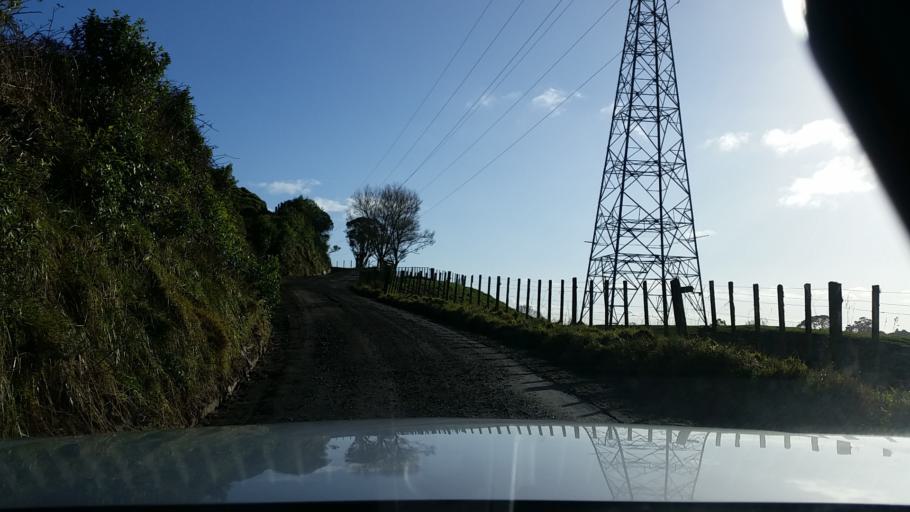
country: NZ
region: Taranaki
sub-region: South Taranaki District
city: Eltham
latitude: -39.4566
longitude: 174.3693
